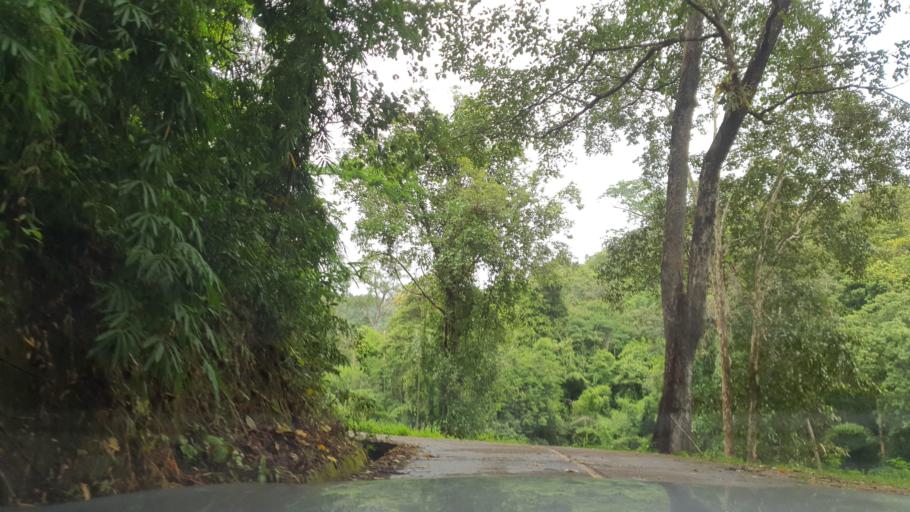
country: TH
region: Chiang Mai
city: Mae Taeng
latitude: 19.2248
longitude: 98.9244
